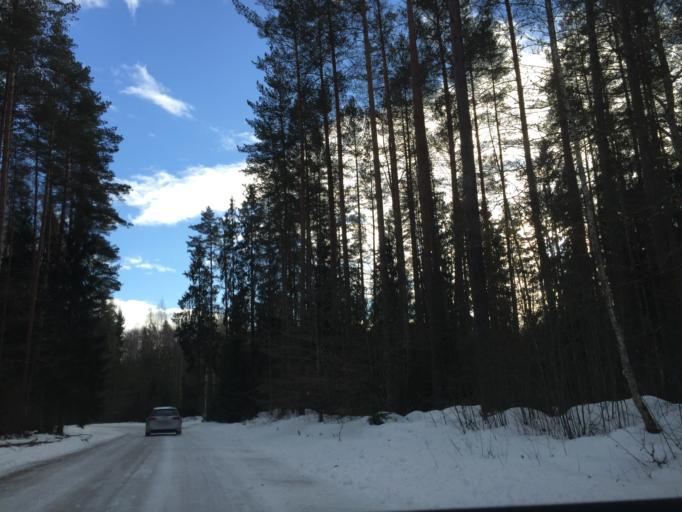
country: LV
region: Lielvarde
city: Lielvarde
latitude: 56.5629
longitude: 24.7987
